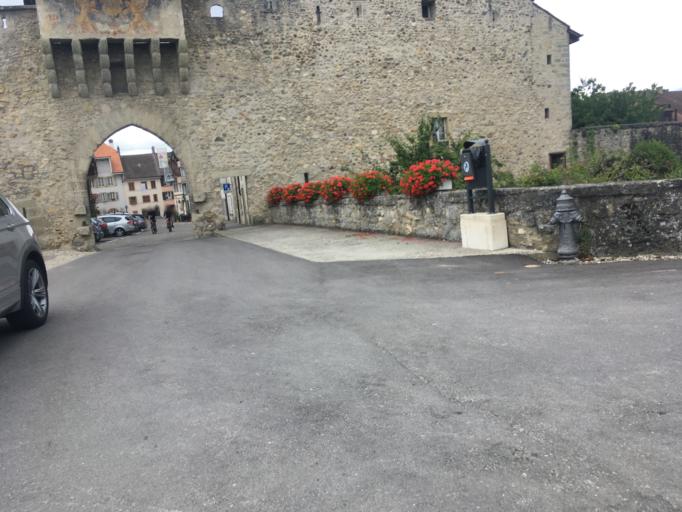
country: CH
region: Fribourg
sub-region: Broye District
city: Estavayer-le-Lac
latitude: 46.8504
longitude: 6.8501
